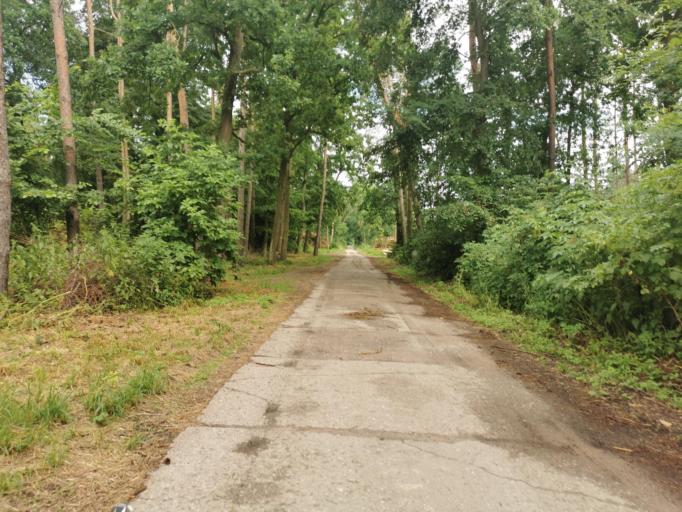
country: SK
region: Trnavsky
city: Gbely
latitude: 48.7631
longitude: 17.0781
